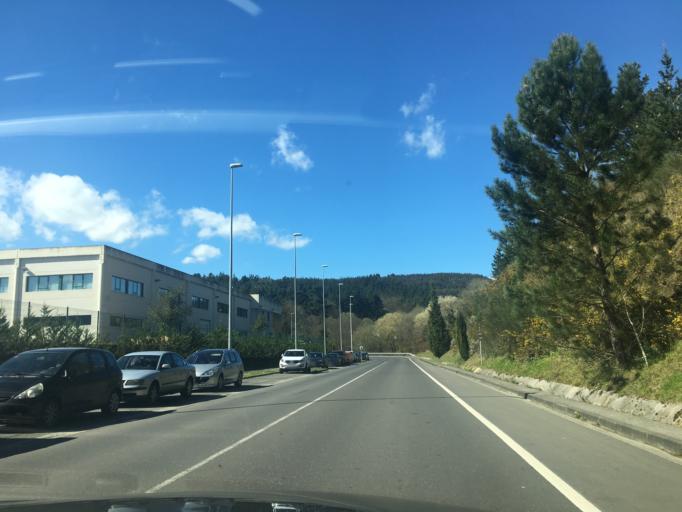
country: ES
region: Basque Country
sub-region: Bizkaia
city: Amorebieta
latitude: 43.2364
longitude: -2.7615
